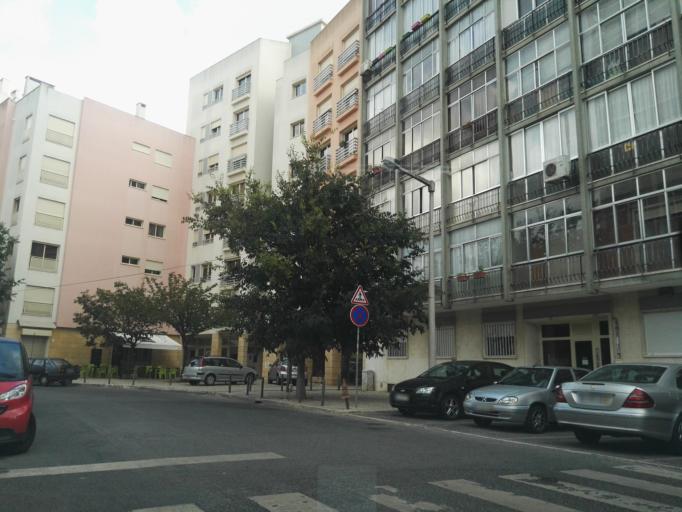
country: PT
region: Lisbon
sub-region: Odivelas
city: Olival do Basto
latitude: 38.7759
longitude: -9.1618
